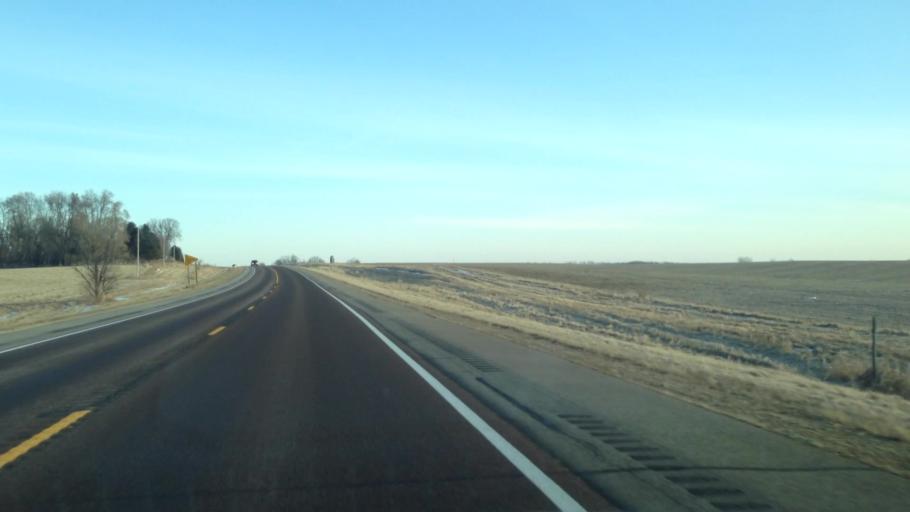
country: US
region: Minnesota
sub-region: Goodhue County
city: Zumbrota
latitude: 44.3283
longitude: -92.6467
